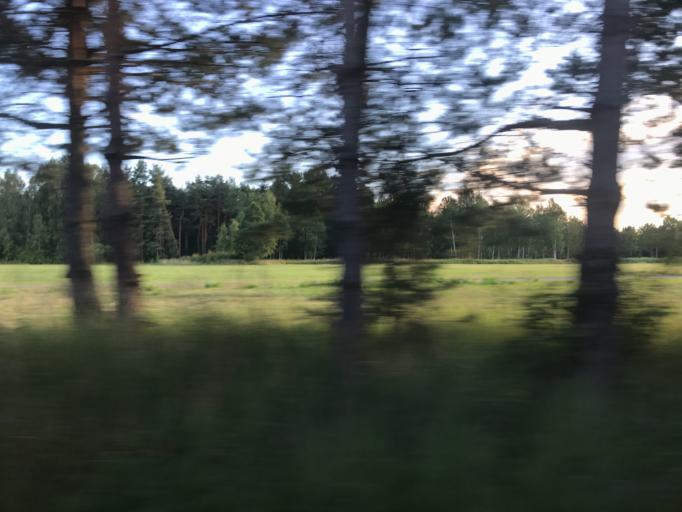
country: CZ
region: Jihocesky
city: Suchdol nad Luznici
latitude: 48.8643
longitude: 14.8865
